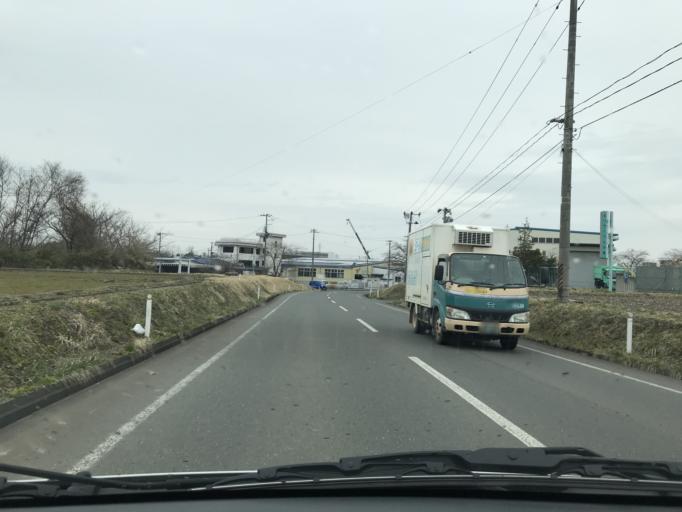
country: JP
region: Iwate
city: Mizusawa
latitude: 39.1772
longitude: 141.1132
